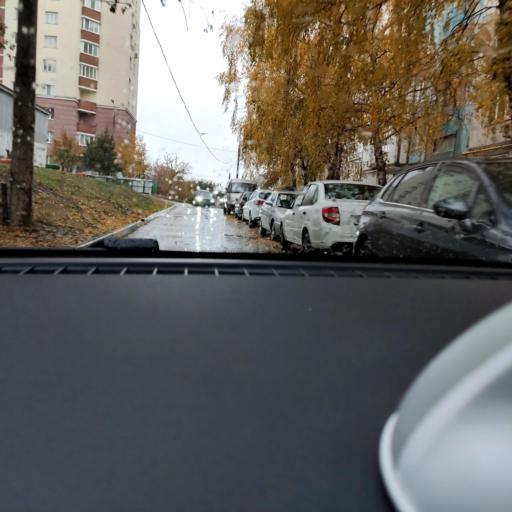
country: RU
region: Samara
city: Samara
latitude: 53.1918
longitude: 50.1488
